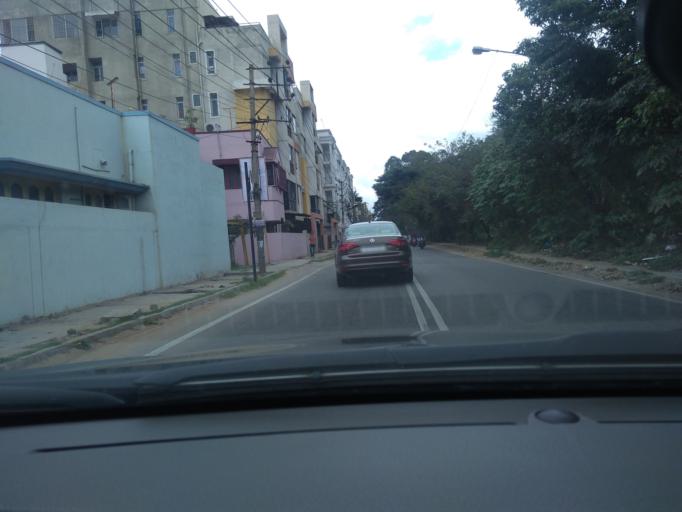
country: IN
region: Karnataka
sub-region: Bangalore Urban
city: Bangalore
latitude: 12.9938
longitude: 77.6570
